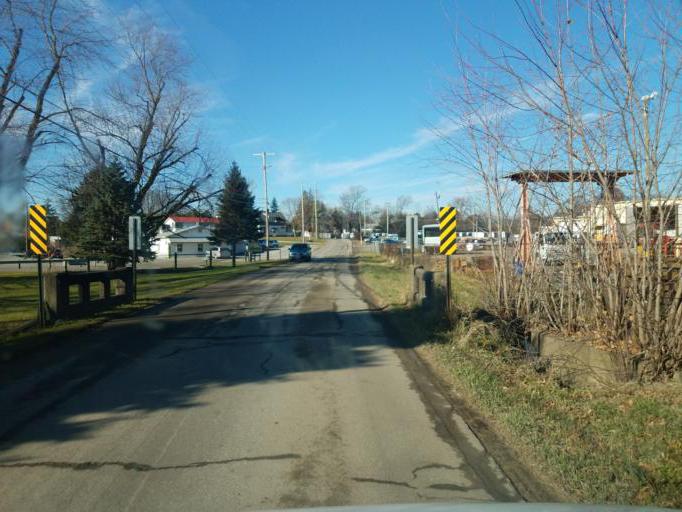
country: US
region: Ohio
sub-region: Wayne County
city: Dalton
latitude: 40.7403
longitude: -81.7415
